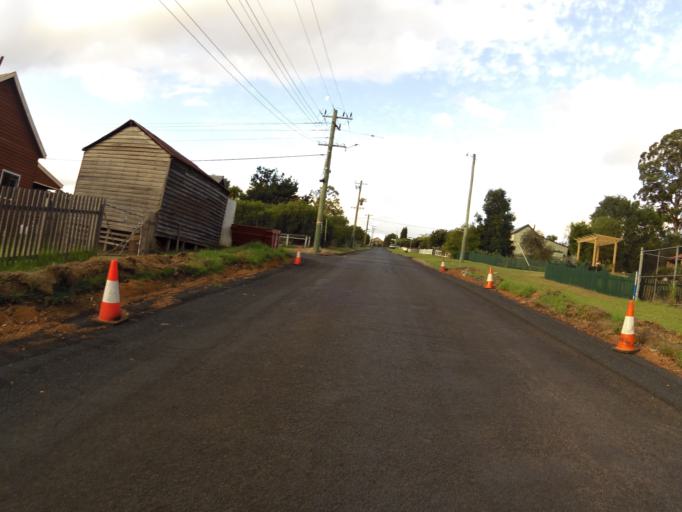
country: AU
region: Western Australia
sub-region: Manjimup
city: Pemberton
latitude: -34.4481
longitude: 116.0322
